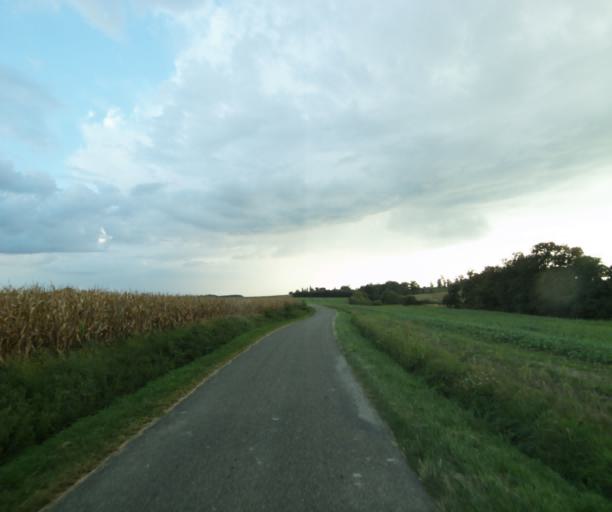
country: FR
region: Midi-Pyrenees
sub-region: Departement du Gers
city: Cazaubon
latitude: 43.9210
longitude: -0.0922
